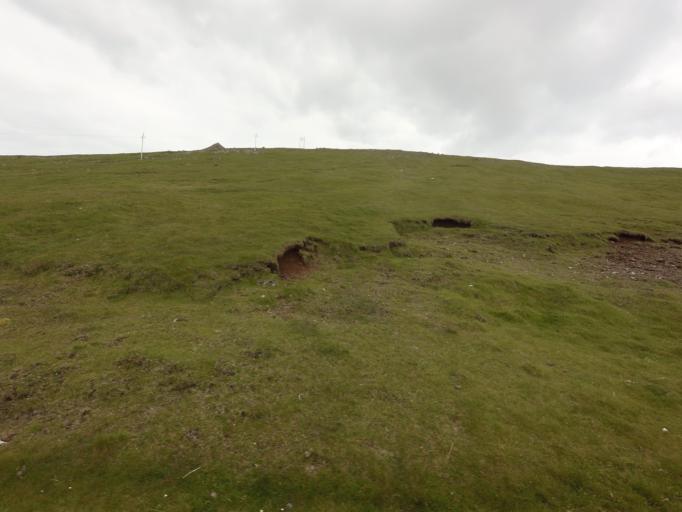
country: FO
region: Suduroy
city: Vagur
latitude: 61.4258
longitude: -6.7537
